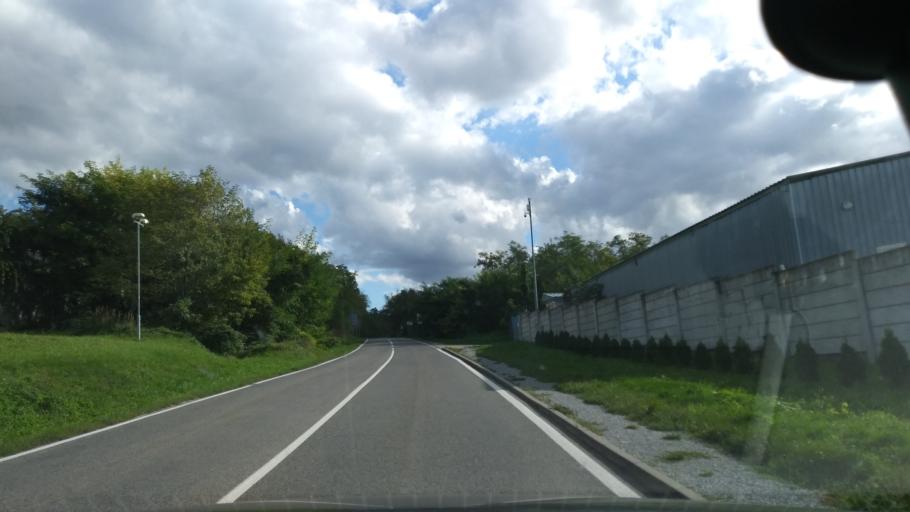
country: SK
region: Trnavsky
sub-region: Okres Skalica
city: Holic
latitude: 48.7985
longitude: 17.1651
